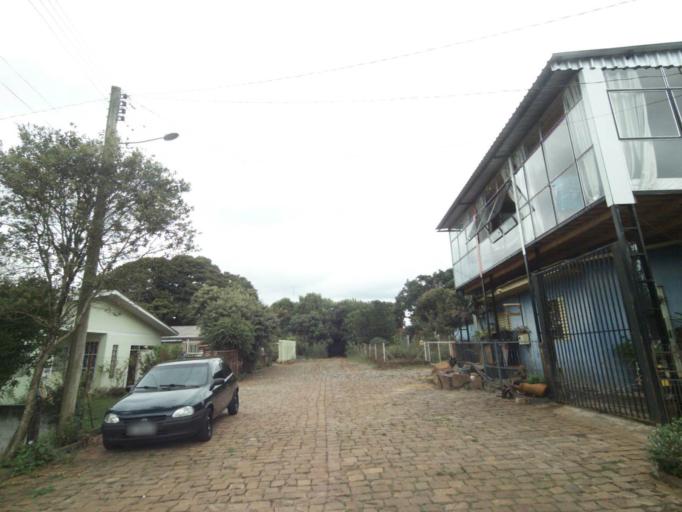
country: BR
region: Rio Grande do Sul
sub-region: Lagoa Vermelha
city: Lagoa Vermelha
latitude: -28.2105
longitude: -51.5310
